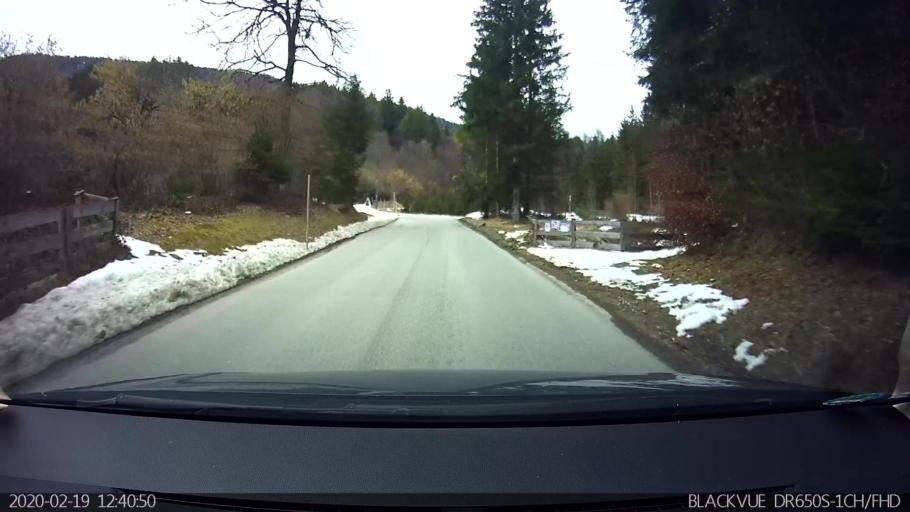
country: AT
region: Tyrol
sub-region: Politischer Bezirk Schwaz
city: Terfens
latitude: 47.3273
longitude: 11.6337
